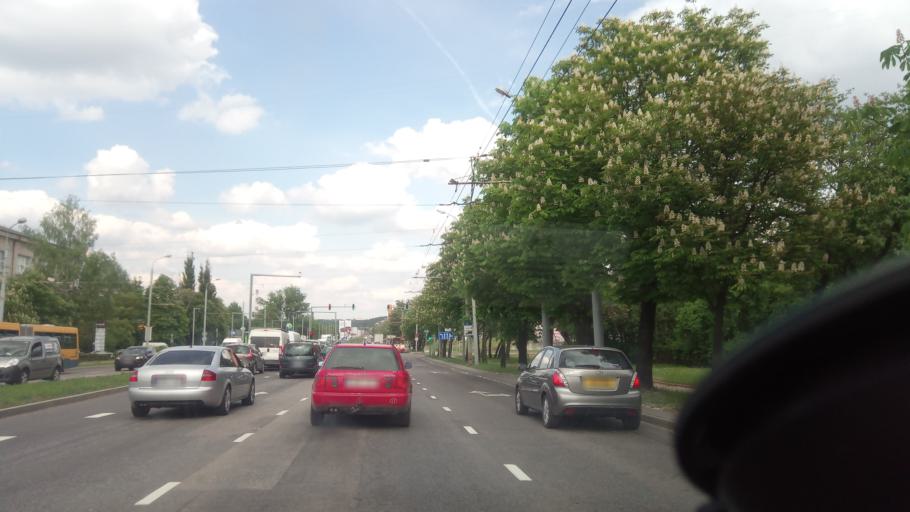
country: LT
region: Vilnius County
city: Lazdynai
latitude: 54.6466
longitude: 25.2066
